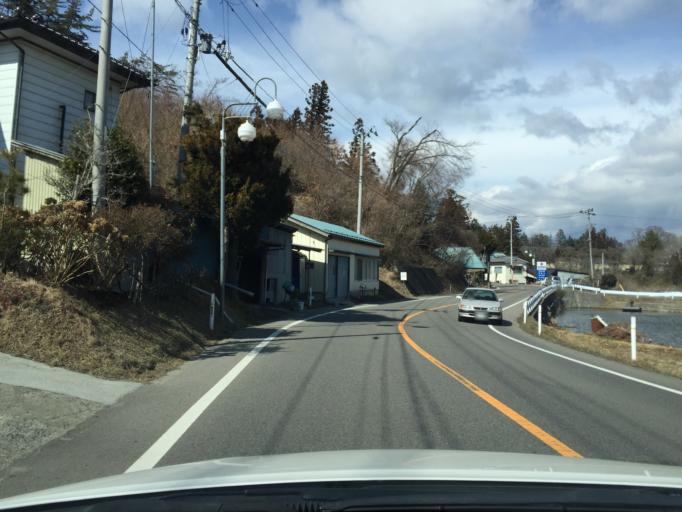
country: JP
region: Fukushima
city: Funehikimachi-funehiki
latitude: 37.3866
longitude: 140.5875
